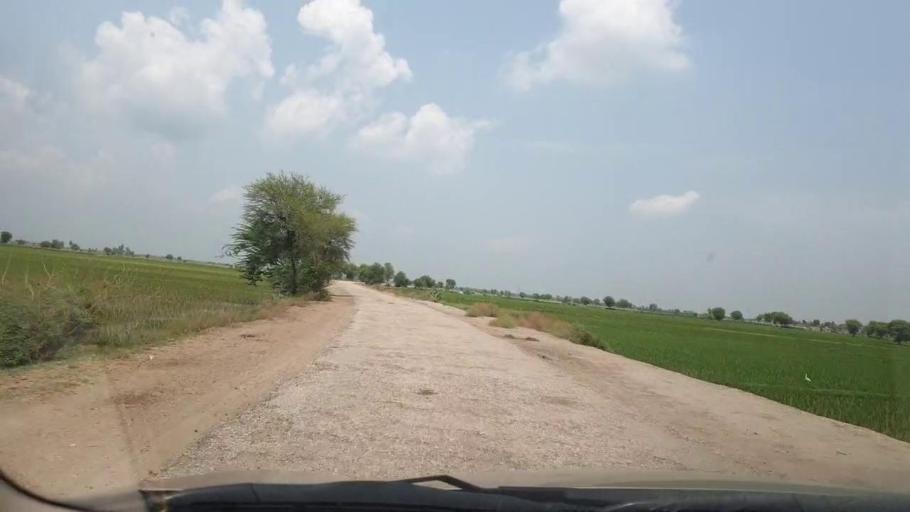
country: PK
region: Sindh
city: Larkana
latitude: 27.6048
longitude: 68.1438
